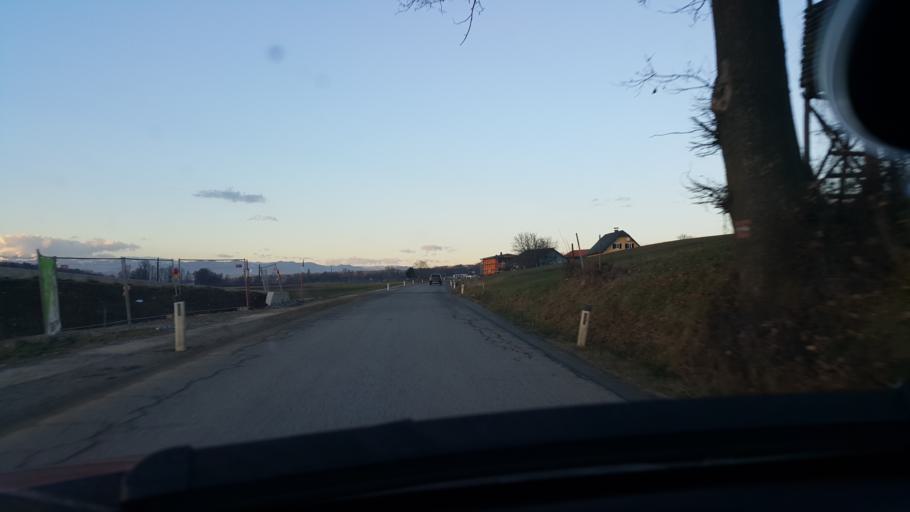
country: AT
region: Styria
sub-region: Politischer Bezirk Graz-Umgebung
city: Lieboch
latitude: 46.9830
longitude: 15.3419
